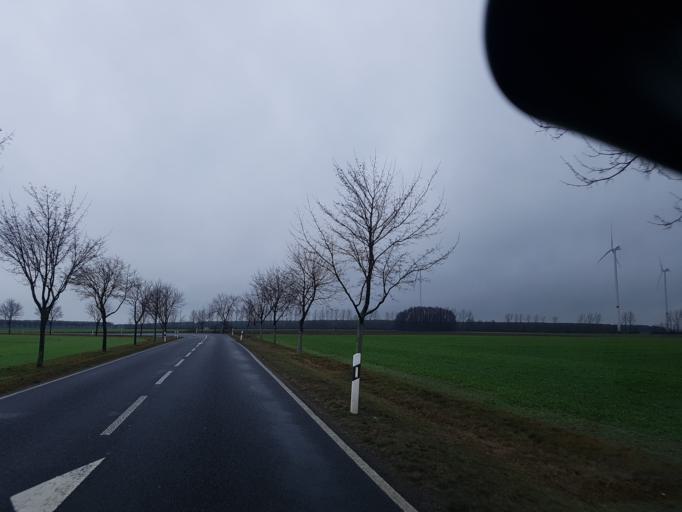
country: DE
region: Brandenburg
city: Bad Liebenwerda
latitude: 51.4575
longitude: 13.3281
